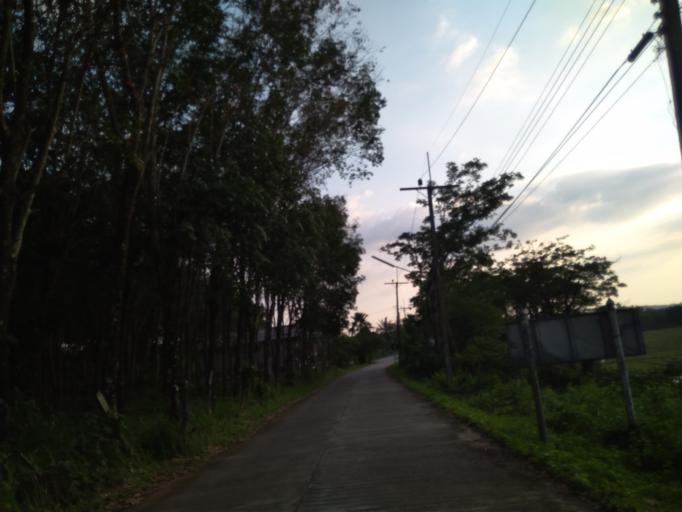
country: TH
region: Phangnga
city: Ko Yao
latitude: 8.1412
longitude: 98.5988
